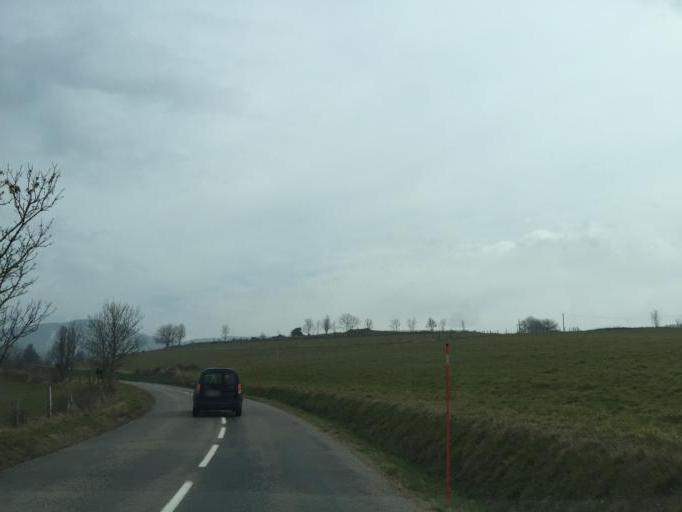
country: FR
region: Rhone-Alpes
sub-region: Departement de la Loire
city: Saint-Chamond
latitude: 45.4109
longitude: 4.5258
